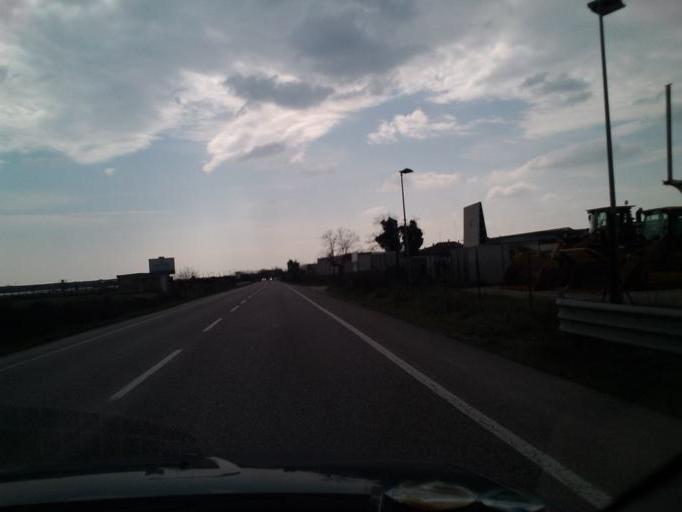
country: IT
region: Veneto
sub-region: Provincia di Verona
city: Sommacampagna
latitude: 45.3985
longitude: 10.8499
